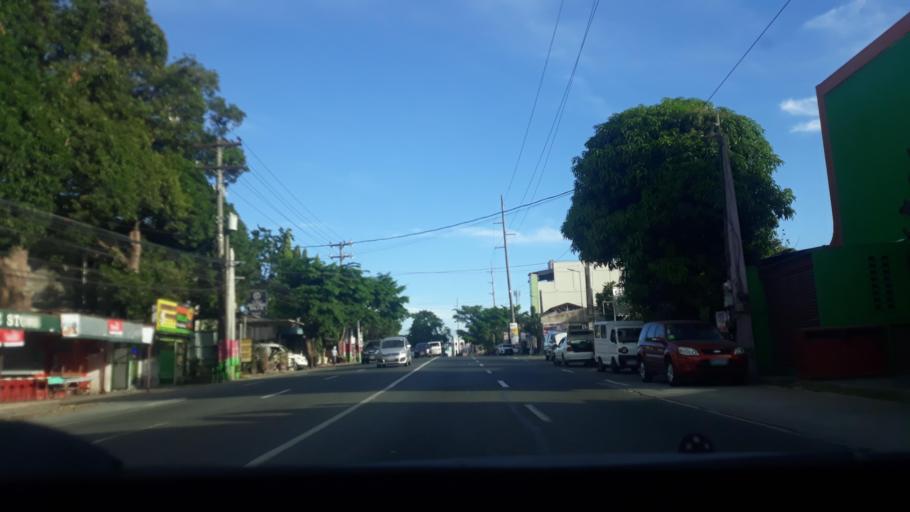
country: PH
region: Calabarzon
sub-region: Province of Cavite
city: Biga
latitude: 14.2614
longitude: 120.9697
